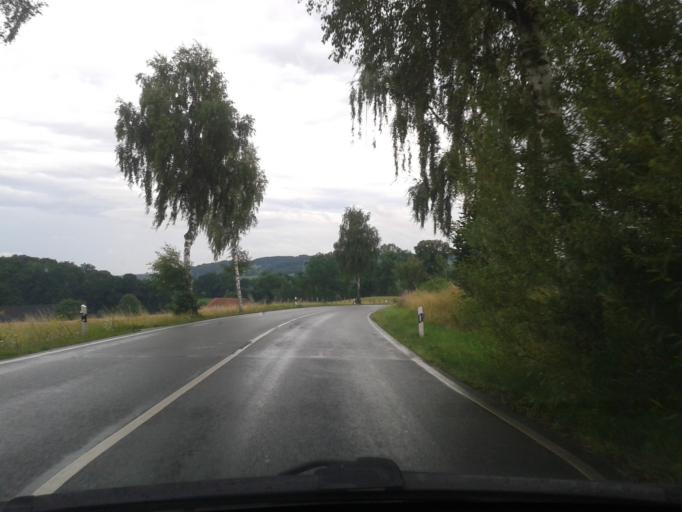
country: DE
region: North Rhine-Westphalia
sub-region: Regierungsbezirk Detmold
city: Detmold
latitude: 51.9787
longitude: 8.8953
